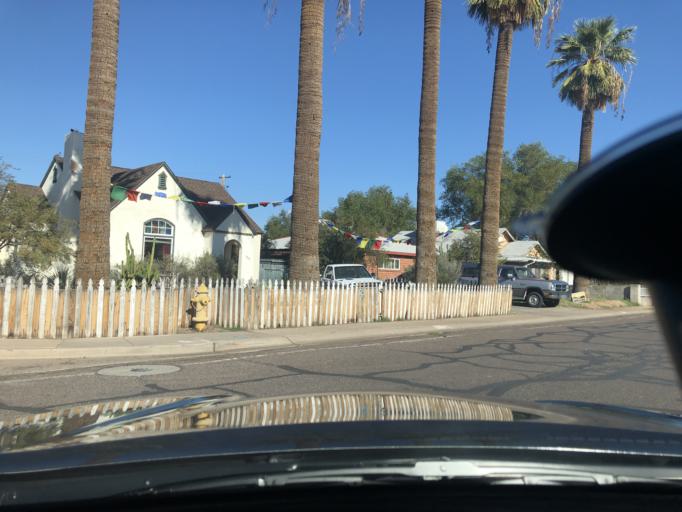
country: US
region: Arizona
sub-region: Maricopa County
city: Phoenix
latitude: 33.4712
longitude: -112.0412
